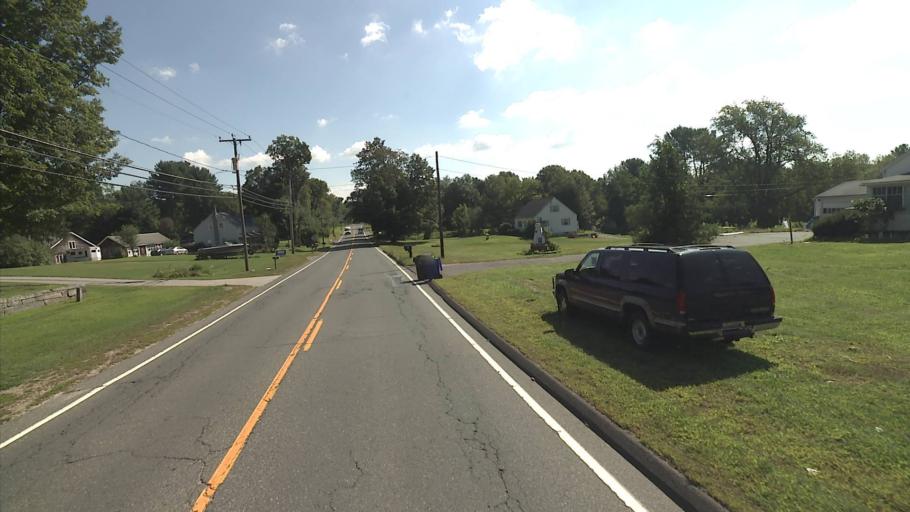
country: US
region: Connecticut
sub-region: Tolland County
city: Stafford Springs
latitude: 41.9694
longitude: -72.3429
